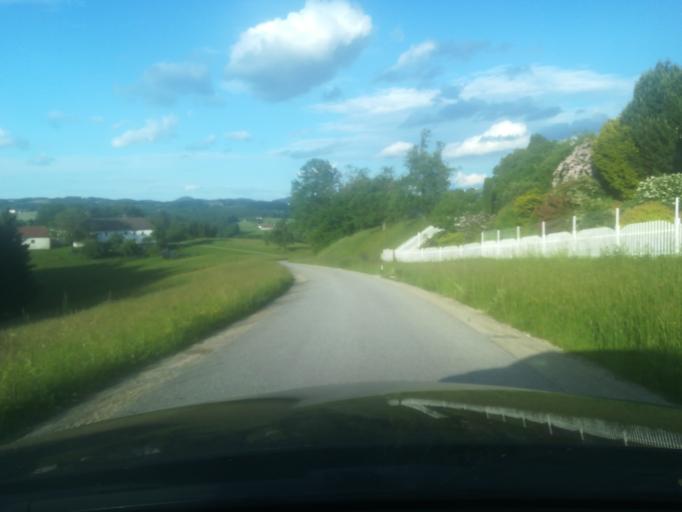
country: AT
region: Upper Austria
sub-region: Politischer Bezirk Perg
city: Perg
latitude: 48.3066
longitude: 14.6029
